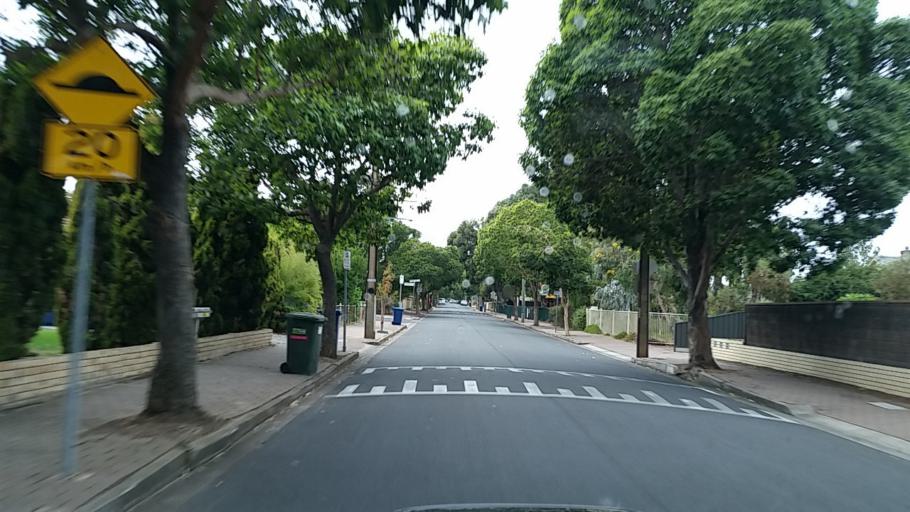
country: AU
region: South Australia
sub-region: Unley
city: Forestville
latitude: -34.9592
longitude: 138.5751
